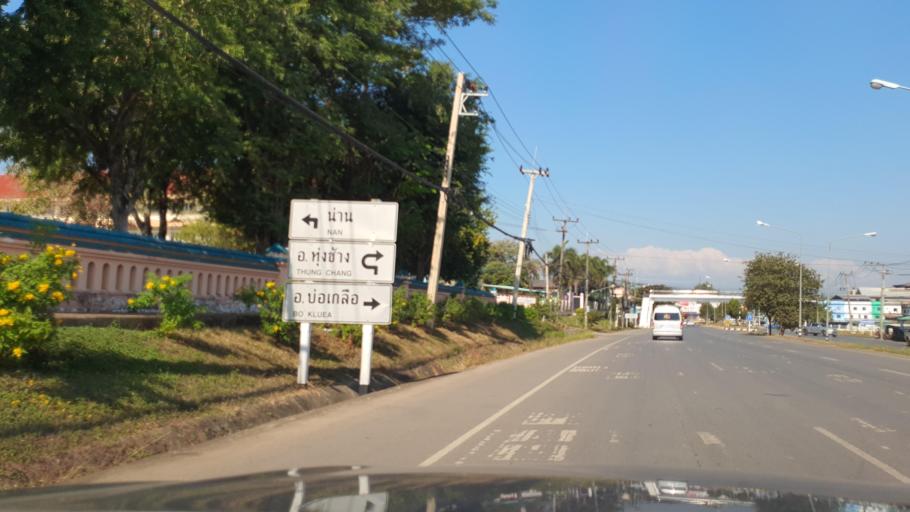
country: TH
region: Nan
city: Pua
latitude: 19.1749
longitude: 100.9170
